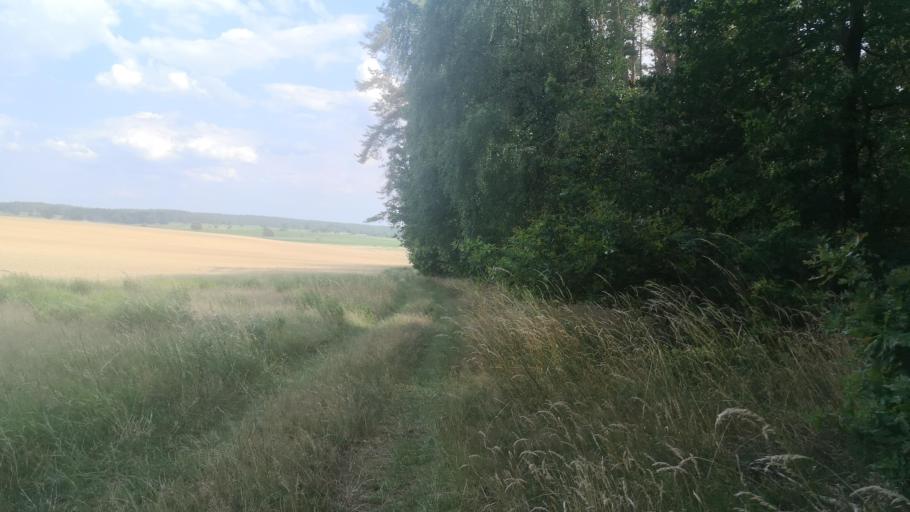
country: DE
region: Lower Saxony
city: Dahlem
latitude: 53.2208
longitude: 10.7444
